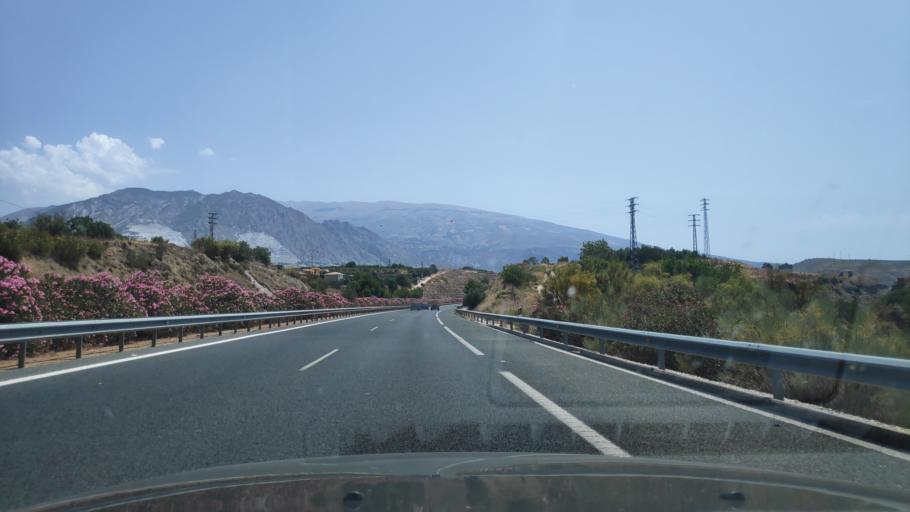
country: ES
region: Andalusia
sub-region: Provincia de Granada
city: Durcal
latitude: 36.9876
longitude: -3.5964
